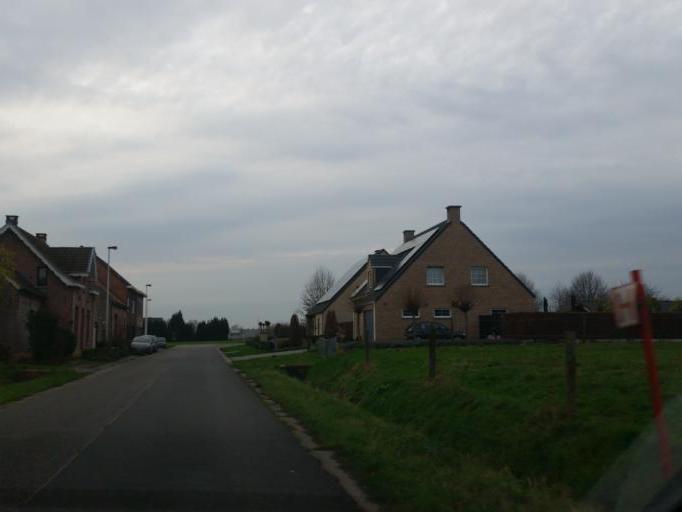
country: BE
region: Flanders
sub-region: Provincie Antwerpen
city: Lier
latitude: 51.1080
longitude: 4.5556
